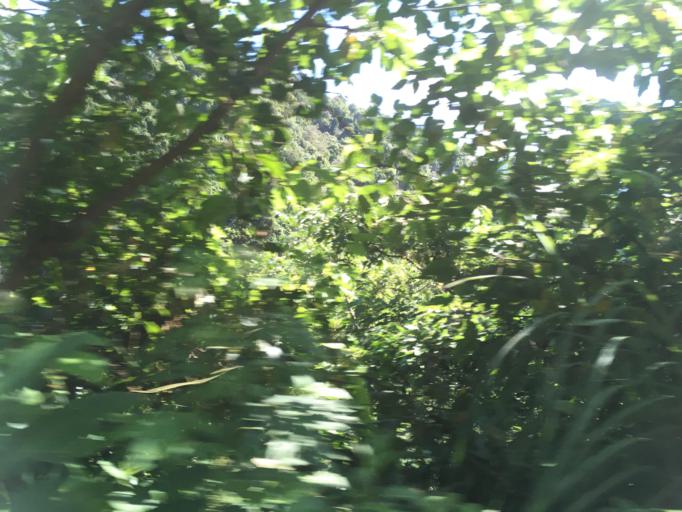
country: TW
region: Taiwan
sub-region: Yilan
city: Yilan
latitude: 24.4245
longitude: 121.7104
